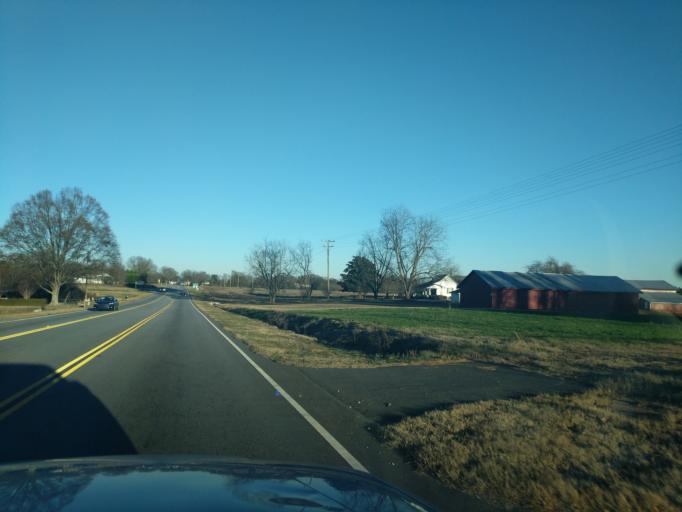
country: US
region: South Carolina
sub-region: Oconee County
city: Seneca
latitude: 34.5939
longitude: -82.9855
